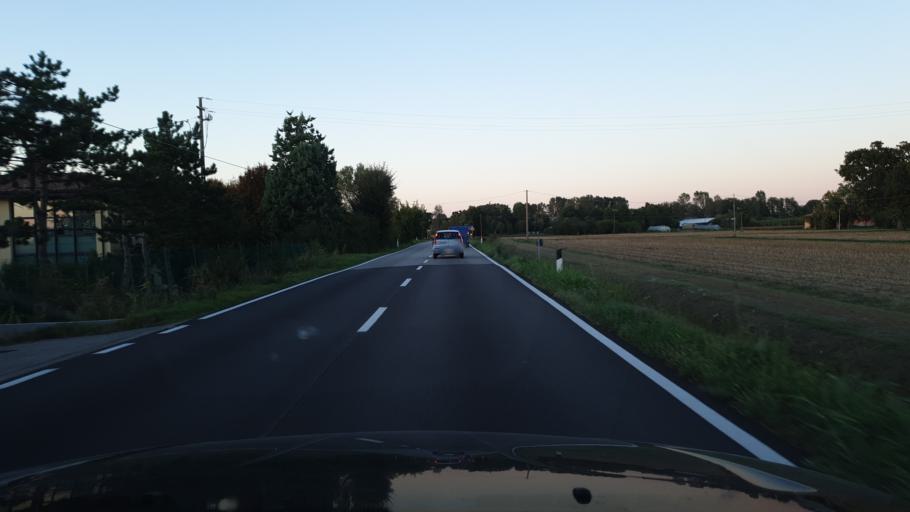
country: IT
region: Emilia-Romagna
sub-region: Provincia di Bologna
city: Ca De Fabbri
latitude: 44.5935
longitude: 11.4344
